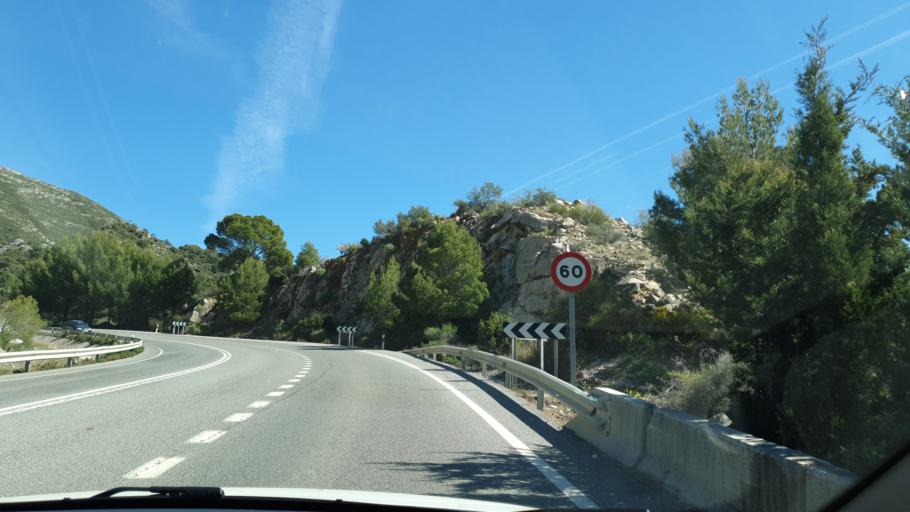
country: ES
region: Andalusia
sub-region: Provincia de Malaga
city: Ojen
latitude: 36.5687
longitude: -4.8639
